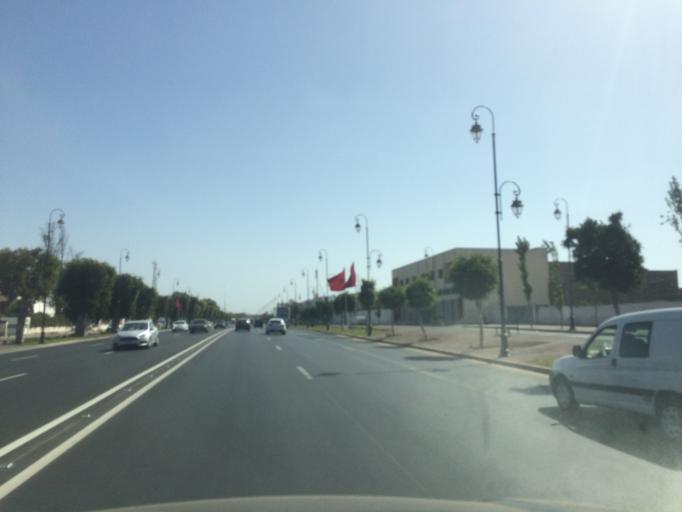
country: MA
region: Rabat-Sale-Zemmour-Zaer
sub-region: Rabat
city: Rabat
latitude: 33.9855
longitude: -6.8702
